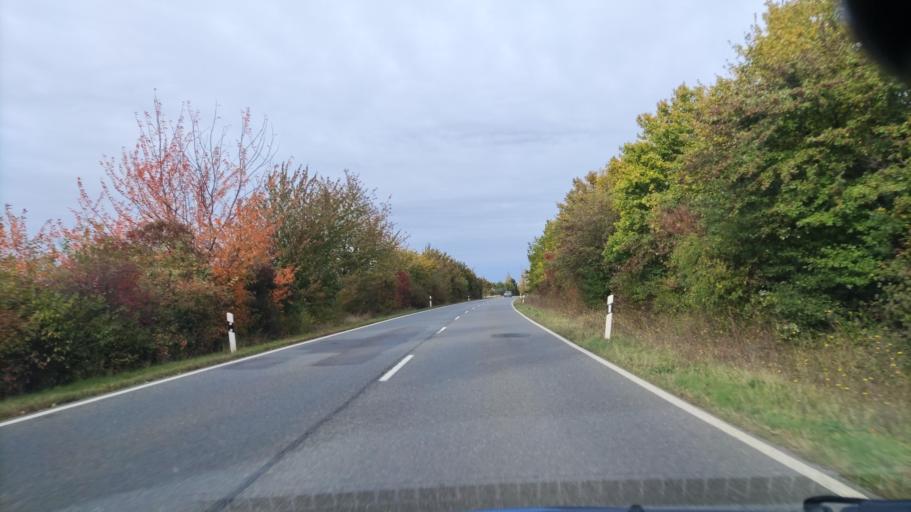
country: DE
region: Saxony-Anhalt
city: Darlingerode
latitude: 51.8652
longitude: 10.7559
